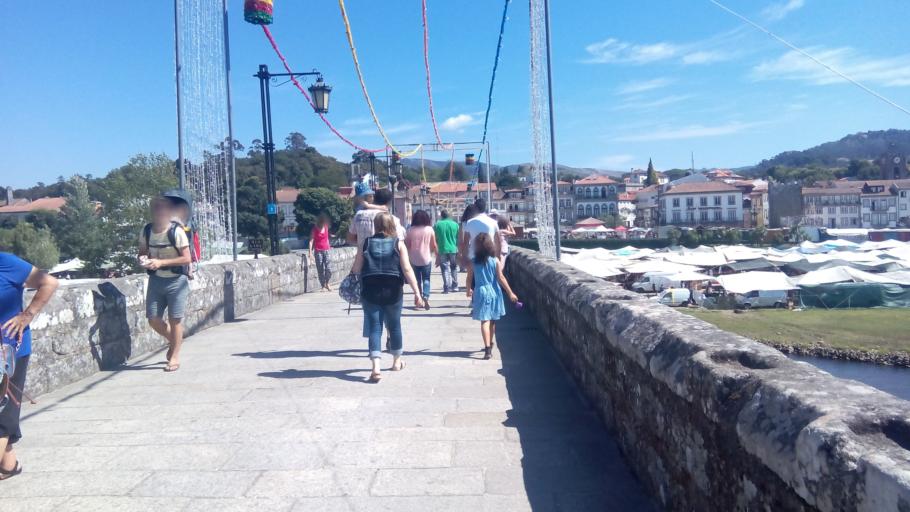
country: PT
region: Viana do Castelo
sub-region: Ponte de Lima
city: Ponte de Lima
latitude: 41.7692
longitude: -8.5864
